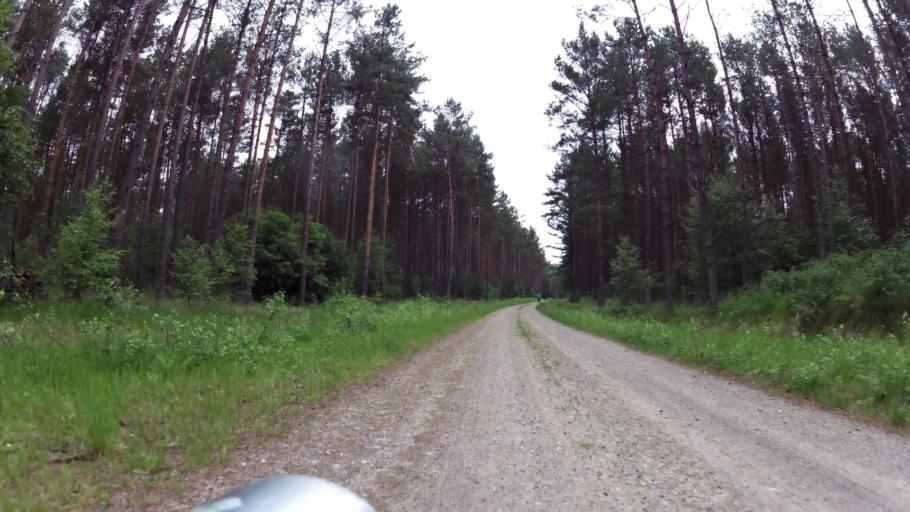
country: PL
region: West Pomeranian Voivodeship
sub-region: Powiat szczecinecki
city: Bialy Bor
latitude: 53.9274
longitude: 16.8355
